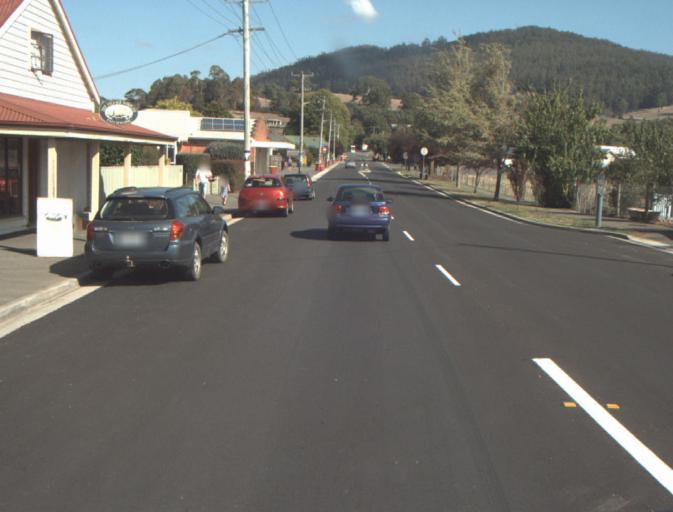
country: AU
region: Tasmania
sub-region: Launceston
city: Mayfield
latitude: -41.2506
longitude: 147.2171
